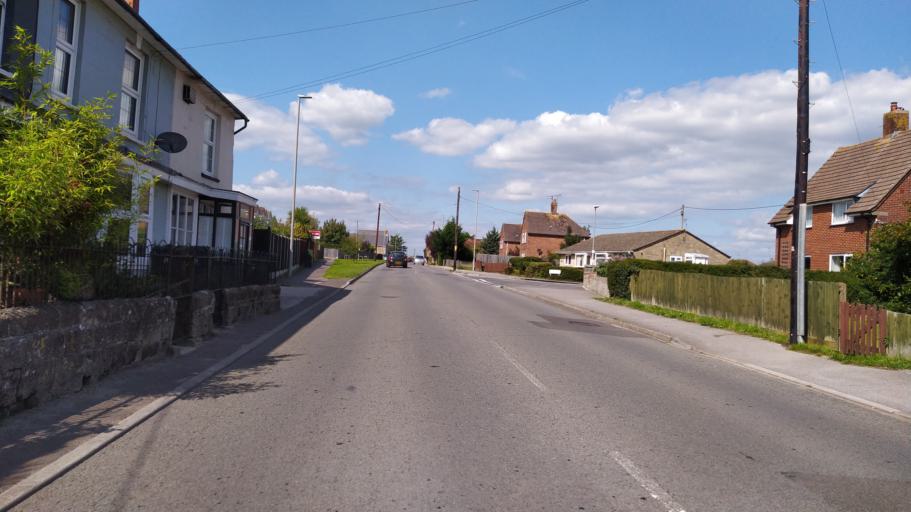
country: GB
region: England
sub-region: Dorset
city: Gillingham
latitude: 51.0442
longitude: -2.2788
